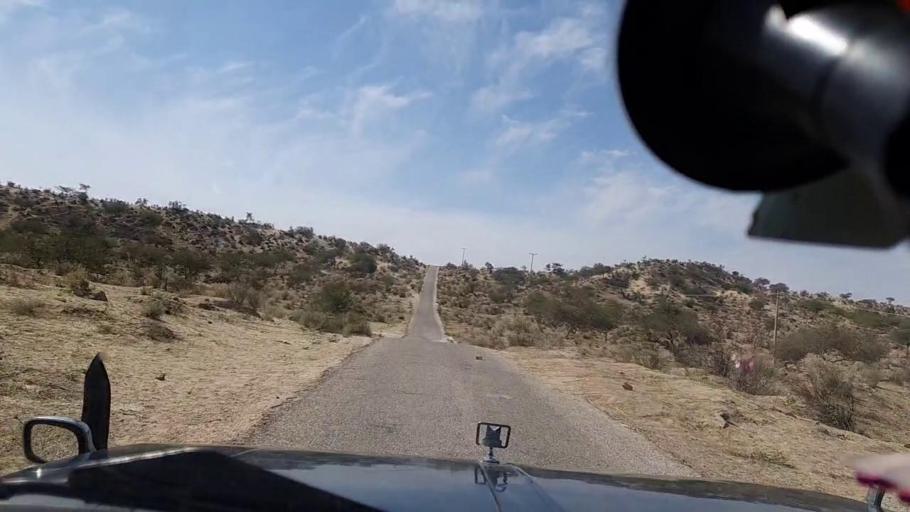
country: PK
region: Sindh
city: Diplo
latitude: 24.3854
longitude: 69.5871
